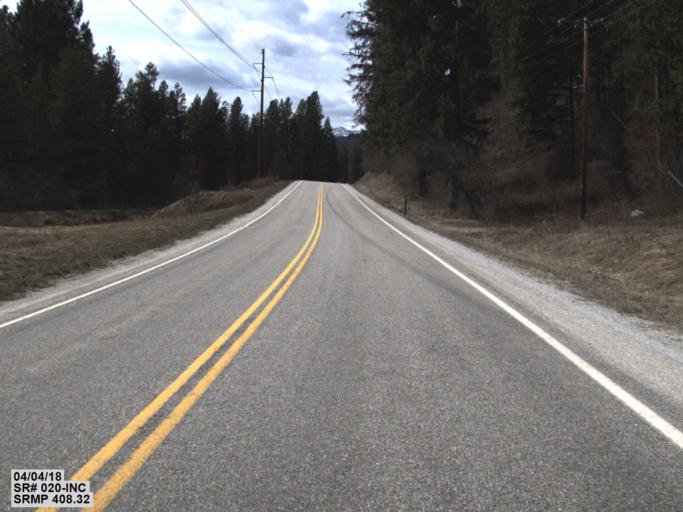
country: US
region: Washington
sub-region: Pend Oreille County
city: Newport
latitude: 48.4745
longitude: -117.2953
